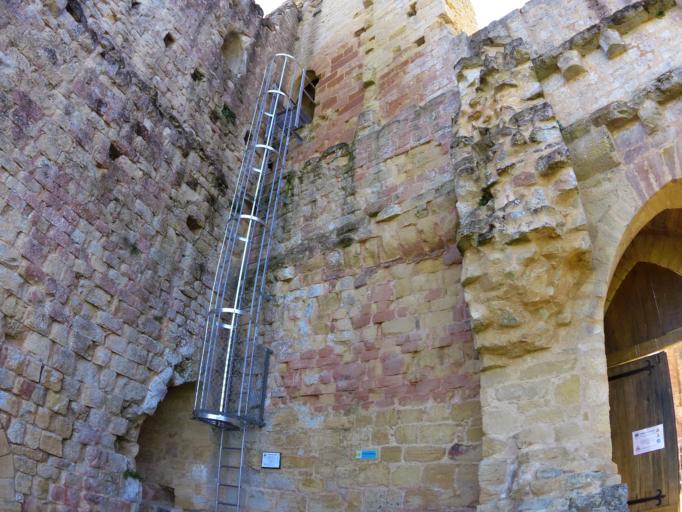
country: FR
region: Aquitaine
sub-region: Departement de la Dordogne
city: Eyvigues-et-Eybenes
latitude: 44.8837
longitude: 1.3528
